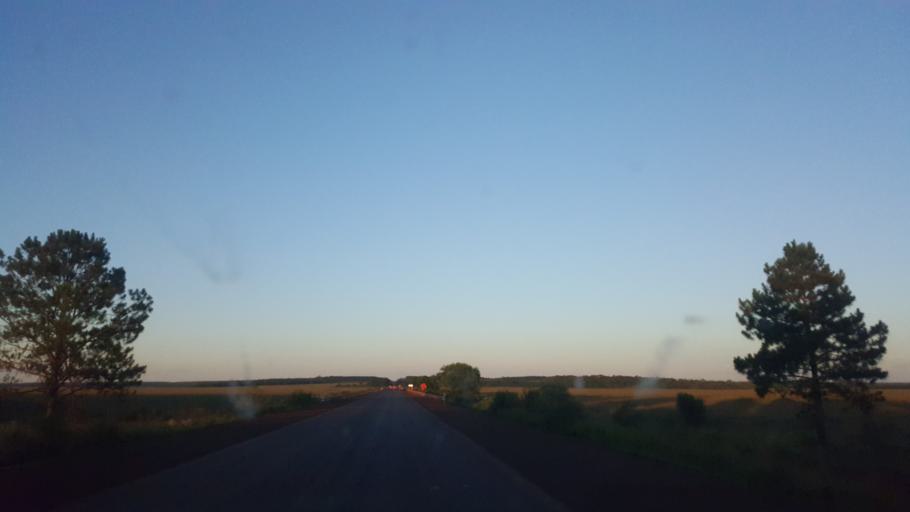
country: AR
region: Corrientes
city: Santo Tome
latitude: -28.3893
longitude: -55.9667
